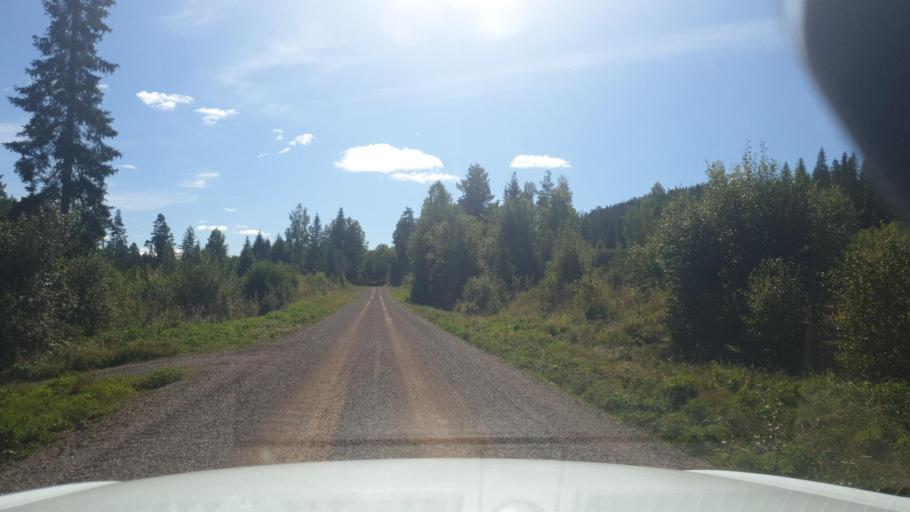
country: SE
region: Vaermland
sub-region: Eda Kommun
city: Charlottenberg
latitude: 60.0795
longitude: 12.5240
